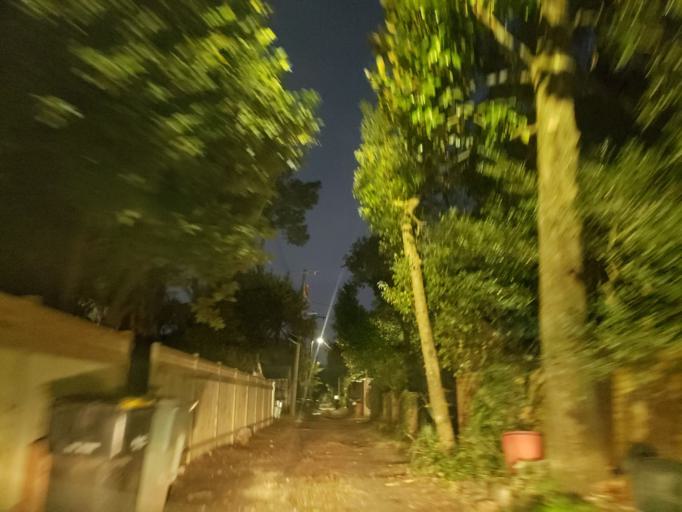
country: US
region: Georgia
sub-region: Chatham County
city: Savannah
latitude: 32.0453
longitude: -81.1010
